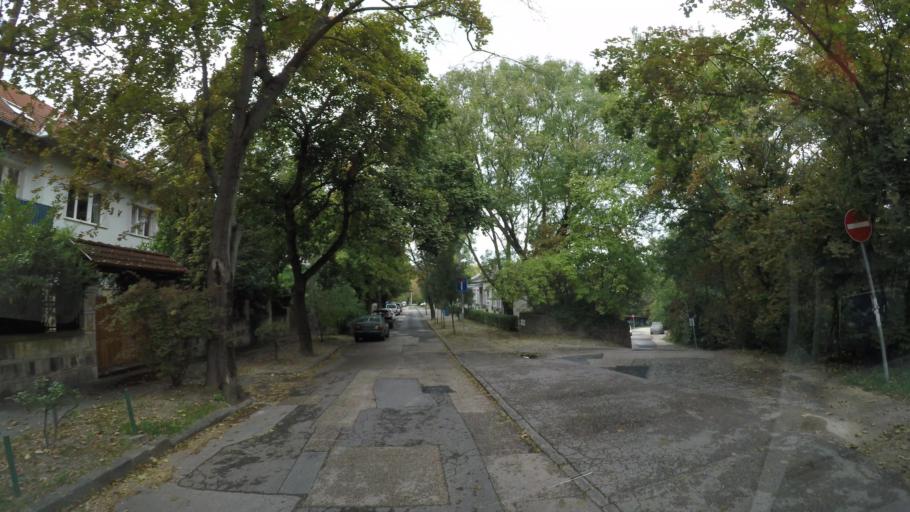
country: HU
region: Budapest
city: Budapest XII. keruelet
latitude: 47.5073
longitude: 19.0110
